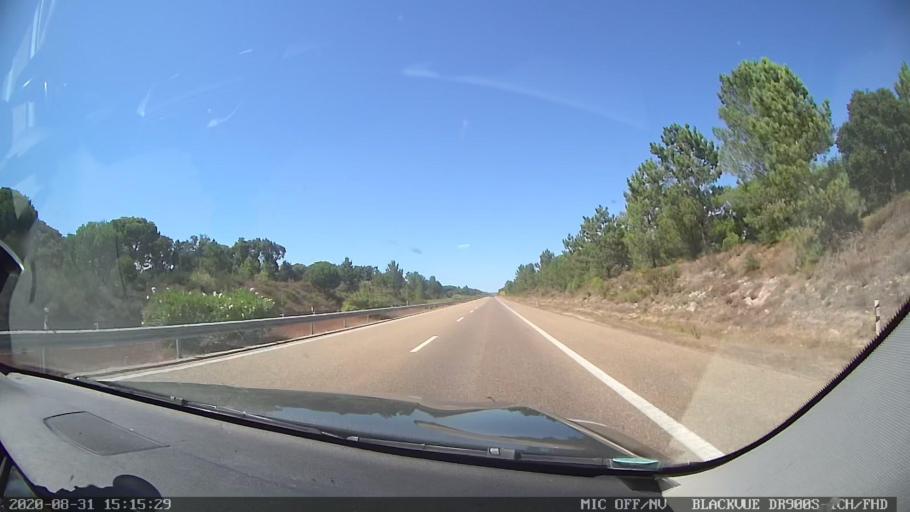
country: PT
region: Evora
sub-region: Vendas Novas
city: Vendas Novas
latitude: 38.6226
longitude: -8.6556
